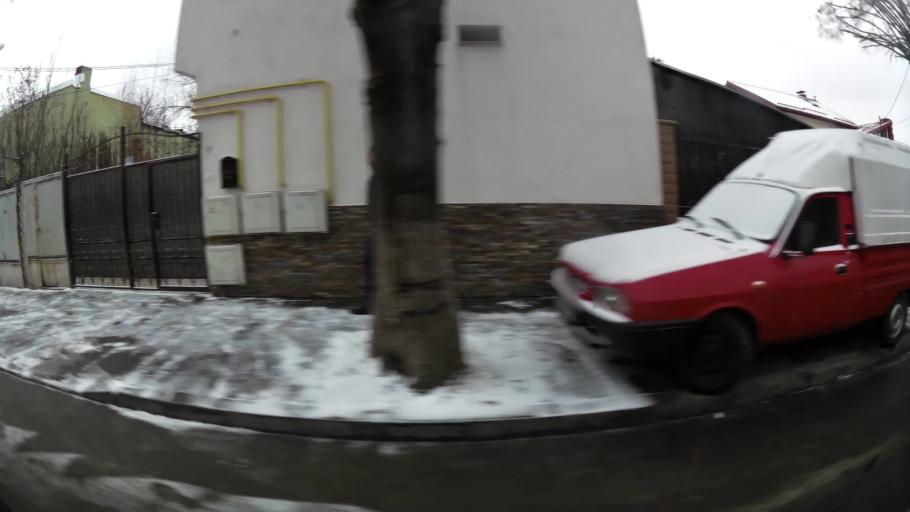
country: RO
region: Prahova
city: Ploiesti
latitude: 44.9358
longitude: 26.0428
